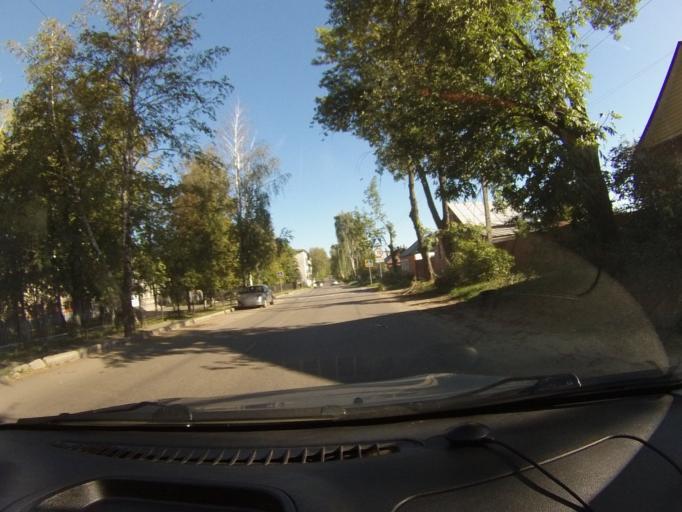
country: RU
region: Tambov
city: Tambov
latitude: 52.7572
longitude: 41.4236
